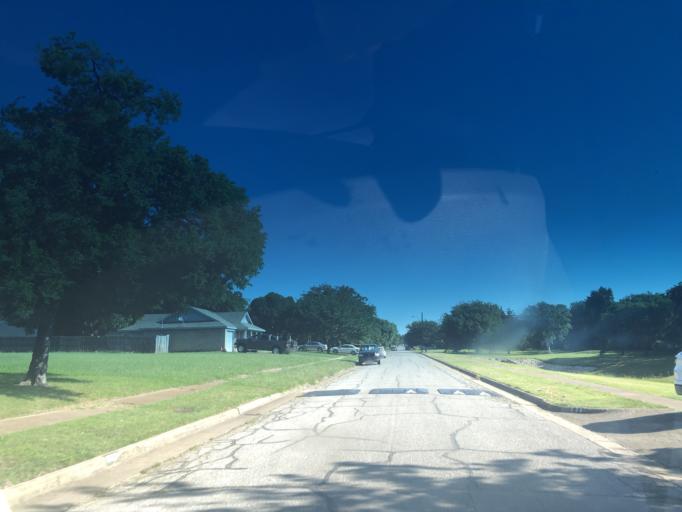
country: US
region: Texas
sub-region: Dallas County
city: Grand Prairie
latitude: 32.7299
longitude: -97.0396
